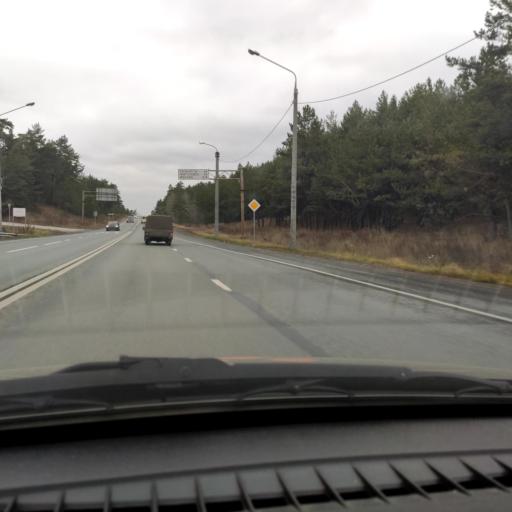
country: RU
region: Samara
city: Volzhskiy
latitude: 53.4397
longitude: 50.1082
